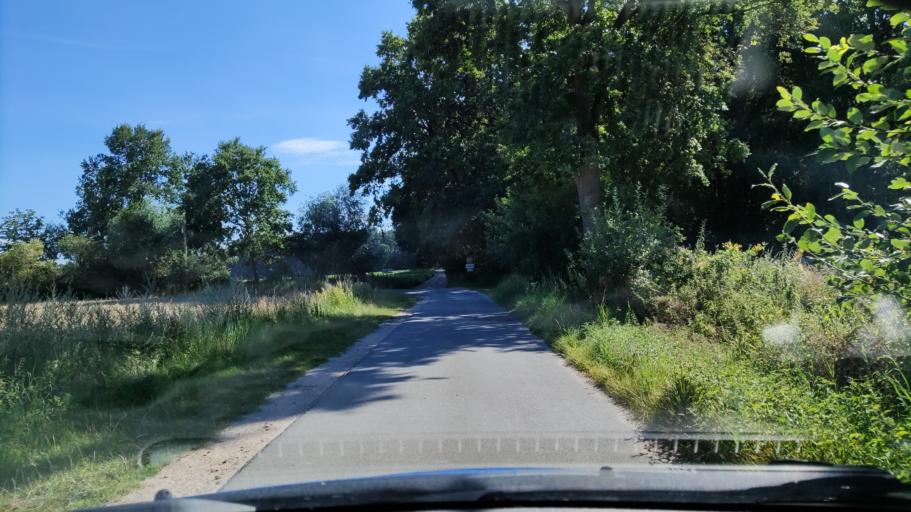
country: DE
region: Lower Saxony
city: Thomasburg
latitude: 53.1869
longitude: 10.6765
